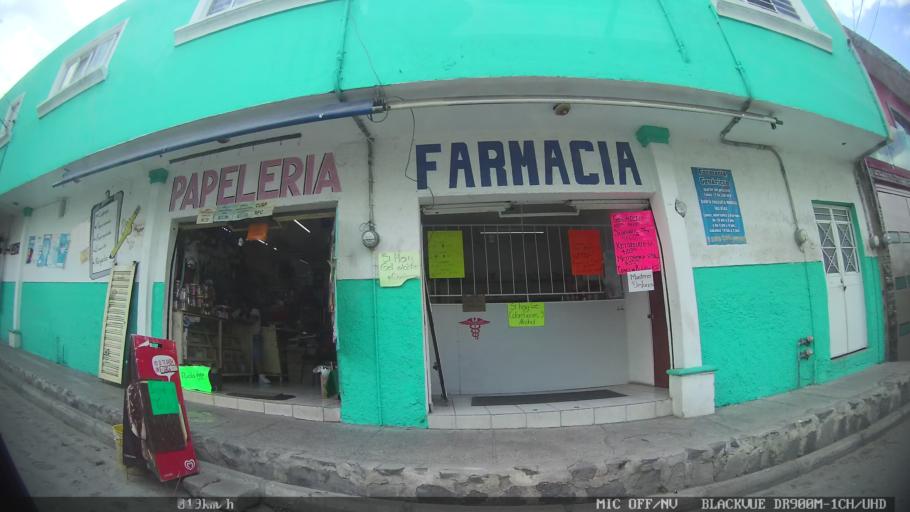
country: MX
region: Jalisco
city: Tlaquepaque
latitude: 20.6368
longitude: -103.2700
